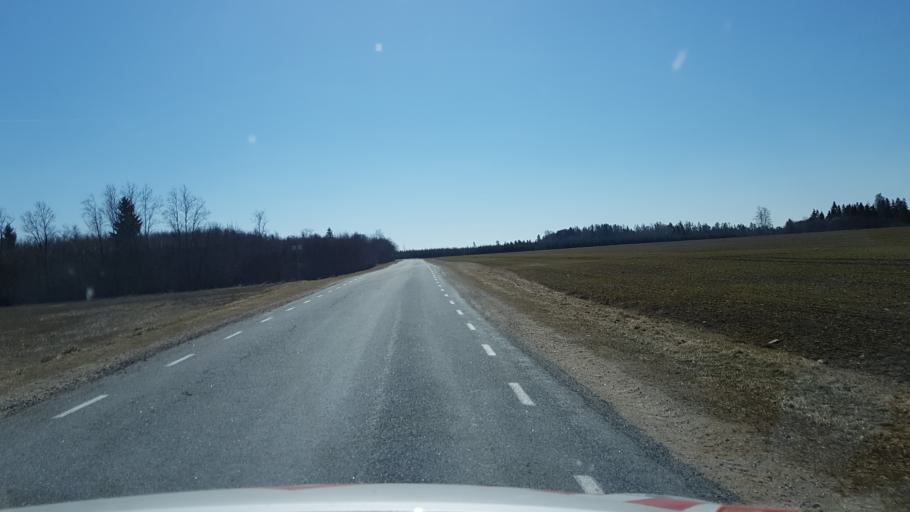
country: EE
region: Laeaene-Virumaa
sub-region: Rakke vald
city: Rakke
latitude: 59.0305
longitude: 26.3498
